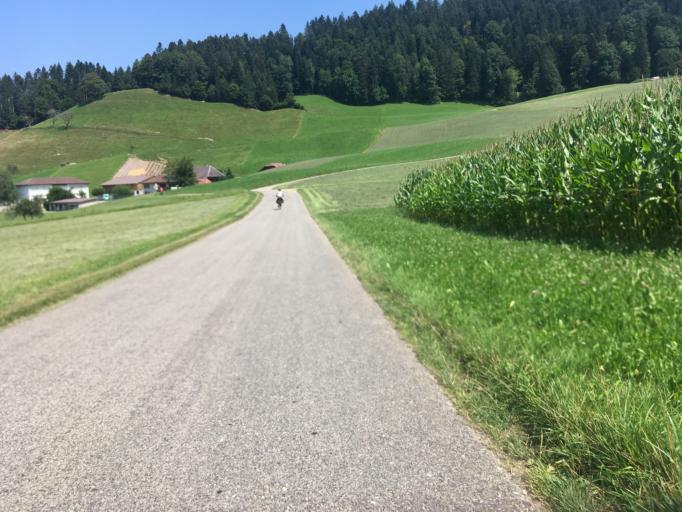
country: CH
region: Bern
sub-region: Bern-Mittelland District
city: Bowil
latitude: 46.8976
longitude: 7.7094
